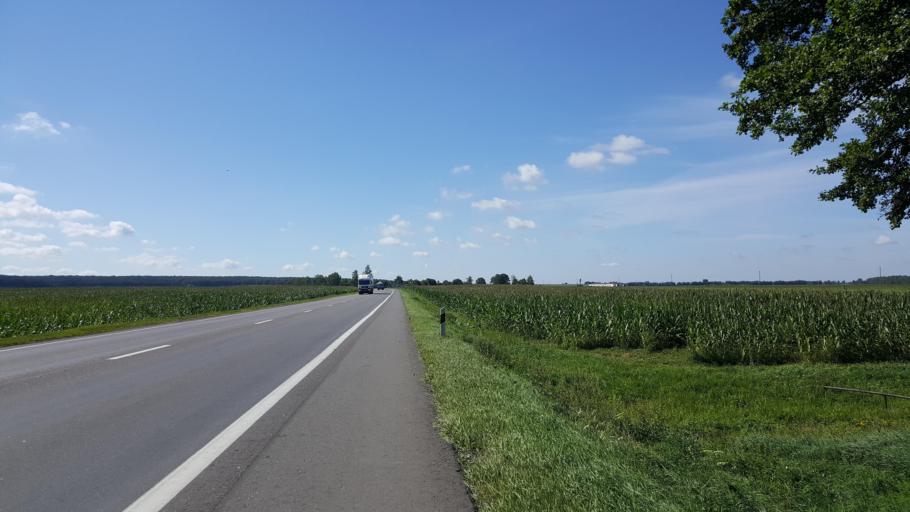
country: BY
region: Brest
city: Kamyanyets
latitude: 52.3149
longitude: 23.7810
